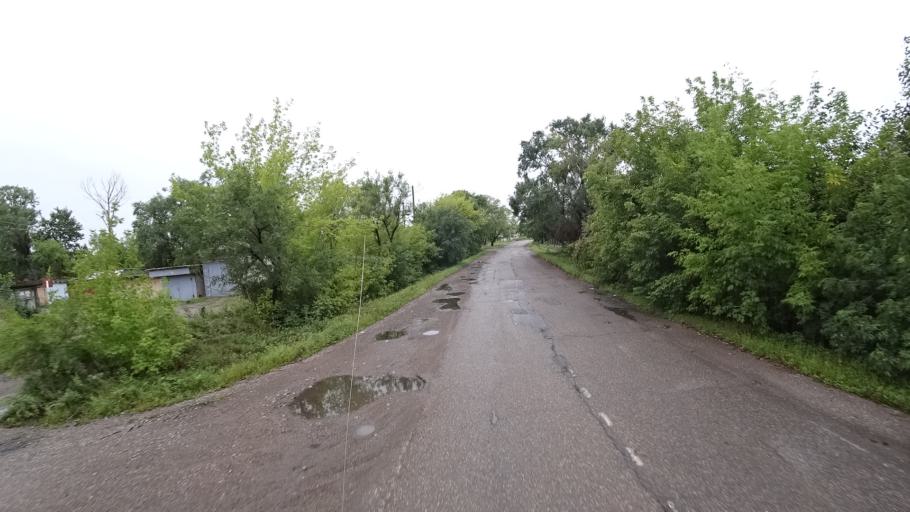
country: RU
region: Primorskiy
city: Monastyrishche
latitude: 44.2012
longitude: 132.4297
